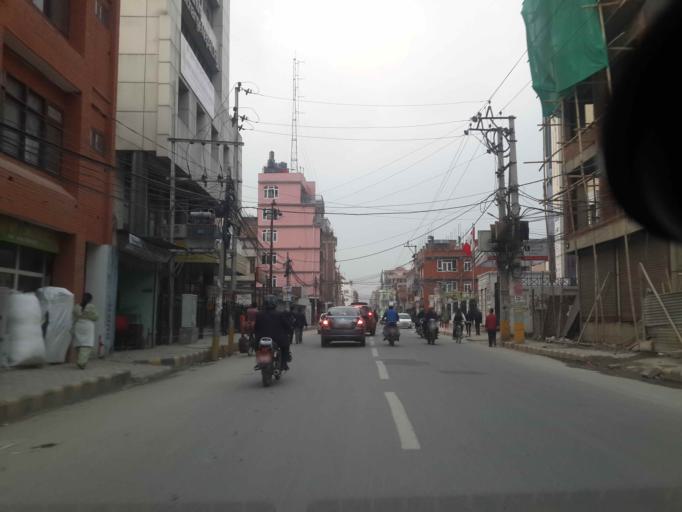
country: NP
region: Central Region
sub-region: Bagmati Zone
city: Kathmandu
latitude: 27.7078
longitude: 85.3273
